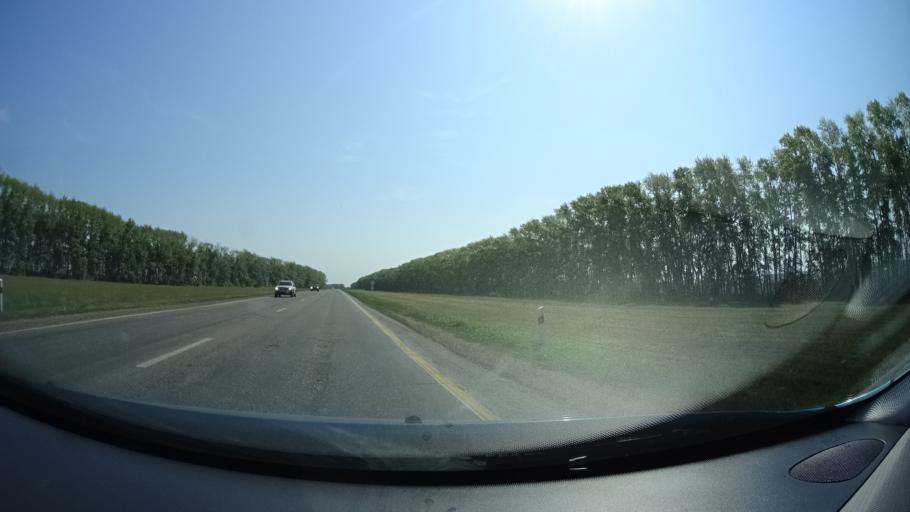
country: RU
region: Bashkortostan
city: Karmaskaly
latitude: 54.3925
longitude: 56.1176
